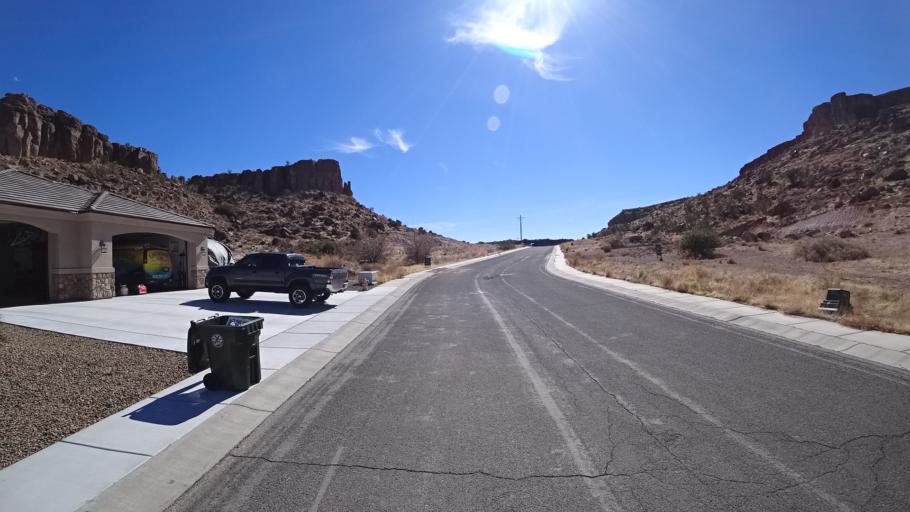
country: US
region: Arizona
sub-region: Mohave County
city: Kingman
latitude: 35.2076
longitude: -114.0551
